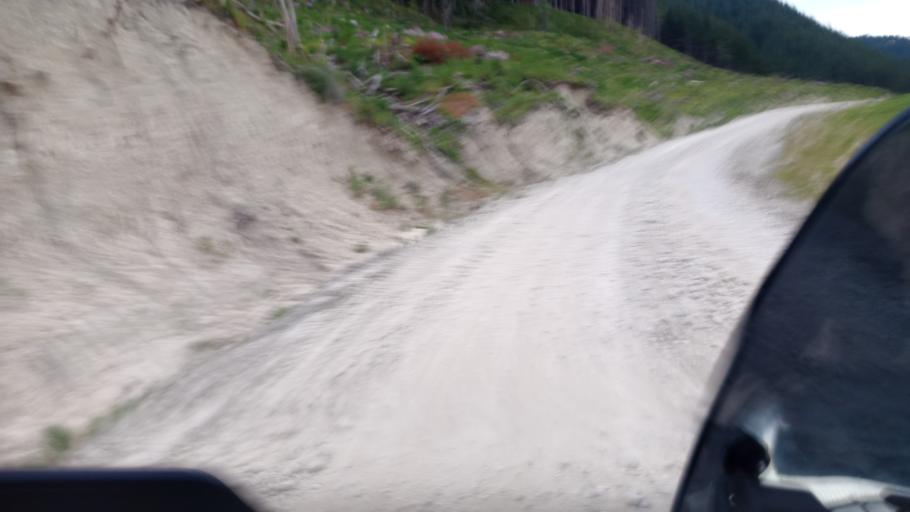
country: NZ
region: Gisborne
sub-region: Gisborne District
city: Gisborne
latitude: -38.4659
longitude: 177.9635
